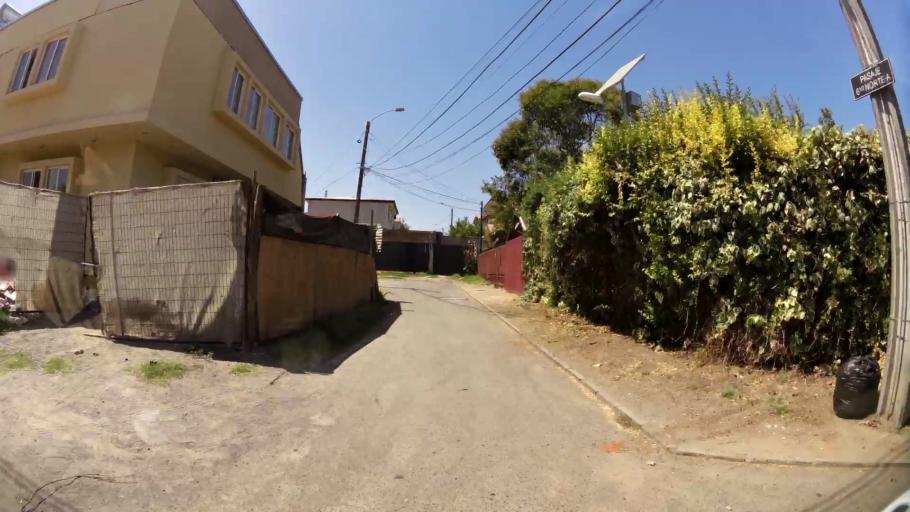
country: CL
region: Maule
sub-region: Provincia de Talca
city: Talca
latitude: -35.4252
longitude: -71.6264
